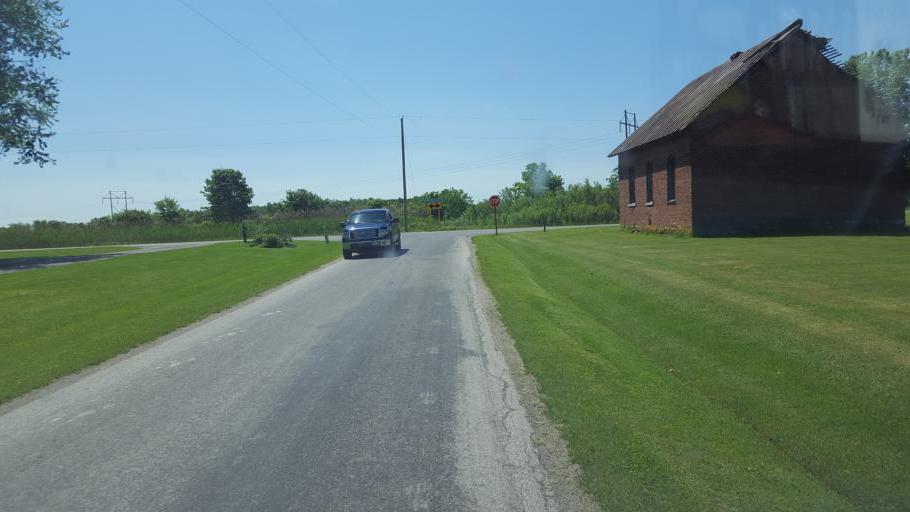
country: US
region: Ohio
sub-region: Union County
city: Richwood
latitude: 40.5713
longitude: -83.4062
